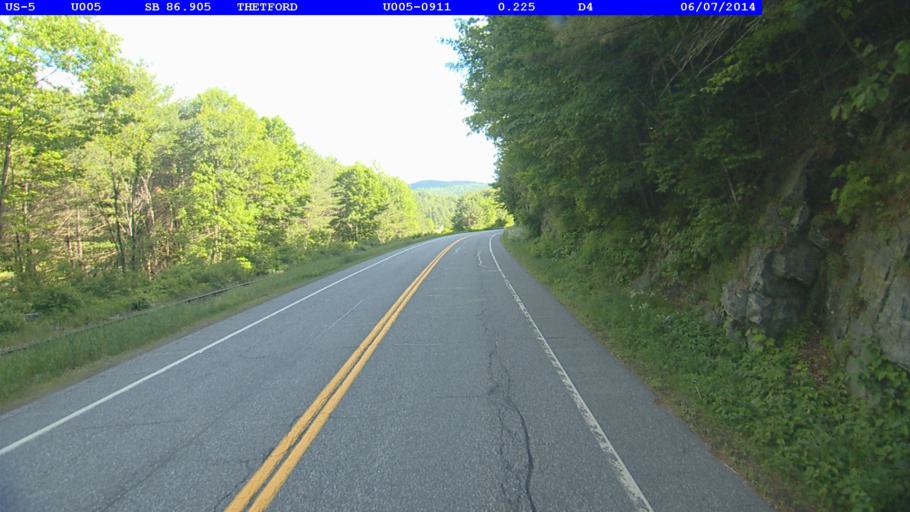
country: US
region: New Hampshire
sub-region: Grafton County
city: Lyme
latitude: 43.7750
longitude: -72.2060
